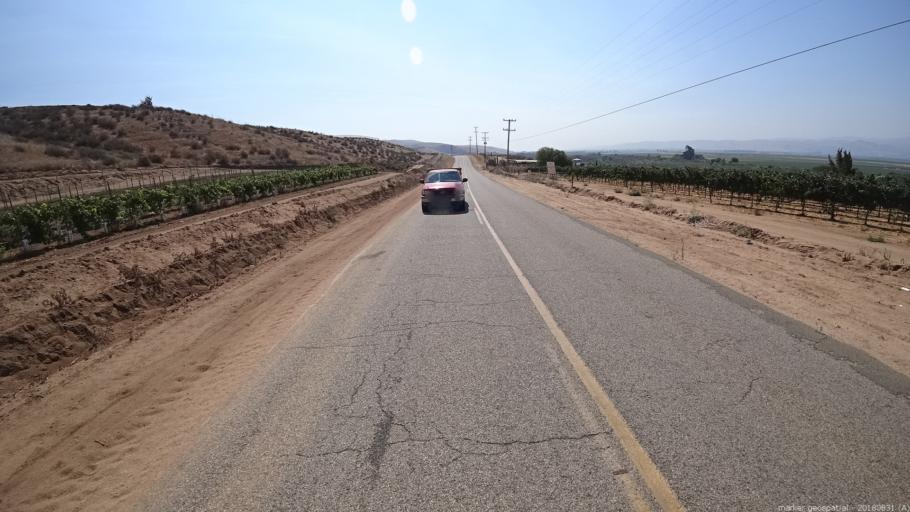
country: US
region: California
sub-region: Monterey County
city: Soledad
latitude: 36.4078
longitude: -121.2649
